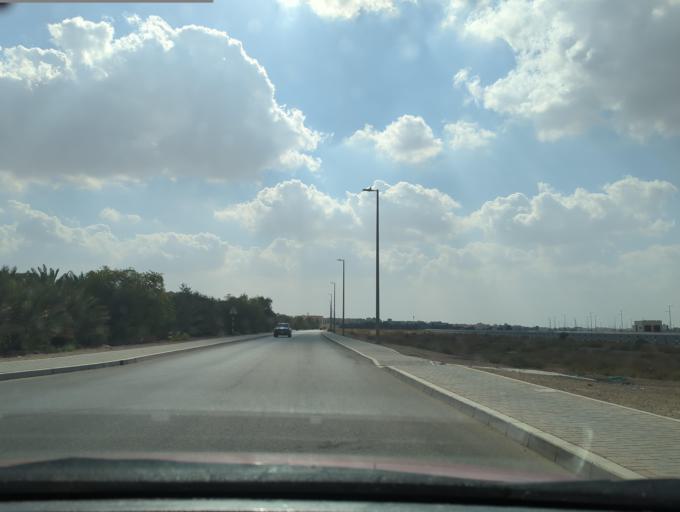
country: AE
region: Abu Dhabi
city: Al Ain
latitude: 24.1616
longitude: 55.6545
